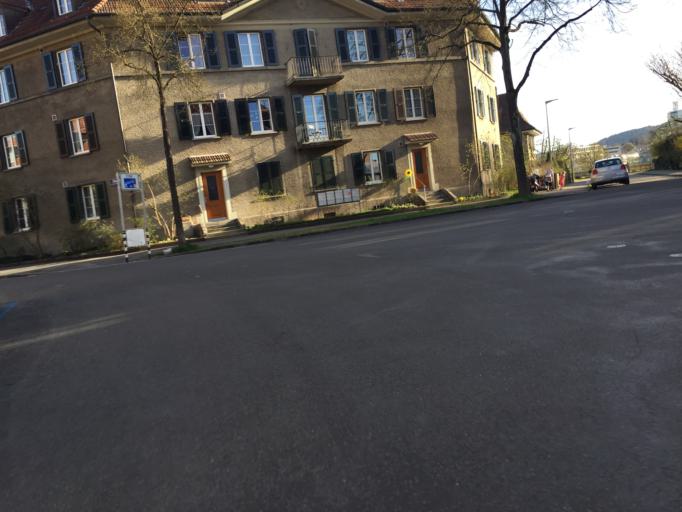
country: CH
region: Bern
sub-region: Bern-Mittelland District
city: Koniz
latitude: 46.9376
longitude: 7.4227
